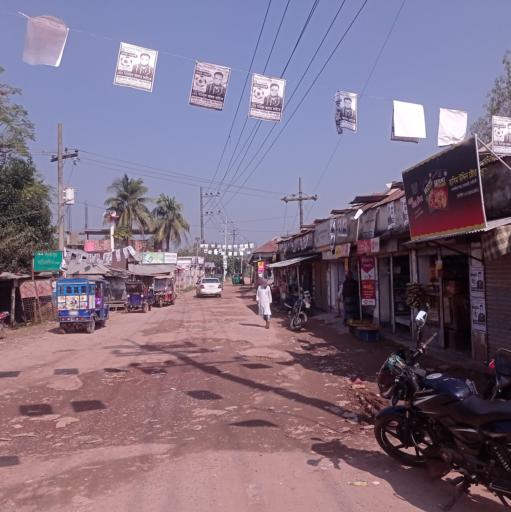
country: BD
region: Dhaka
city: Narsingdi
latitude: 24.0833
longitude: 90.6952
